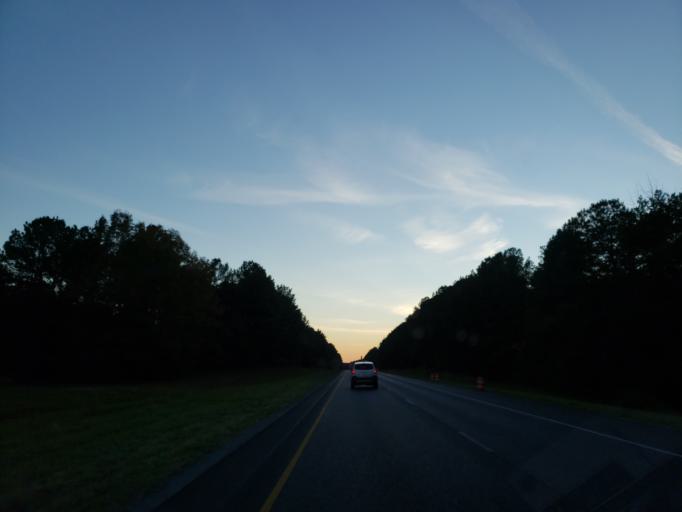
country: US
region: Alabama
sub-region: Sumter County
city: York
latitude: 32.5482
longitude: -88.2732
